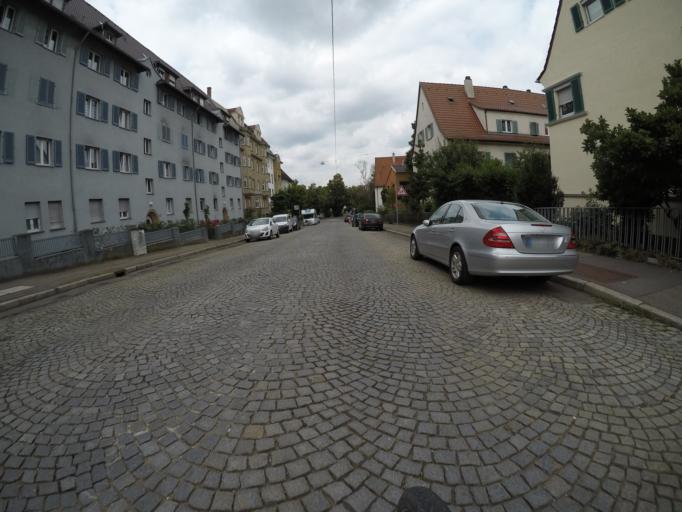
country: DE
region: Baden-Wuerttemberg
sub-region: Regierungsbezirk Stuttgart
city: Stuttgart-Ost
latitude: 48.7906
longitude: 9.2055
